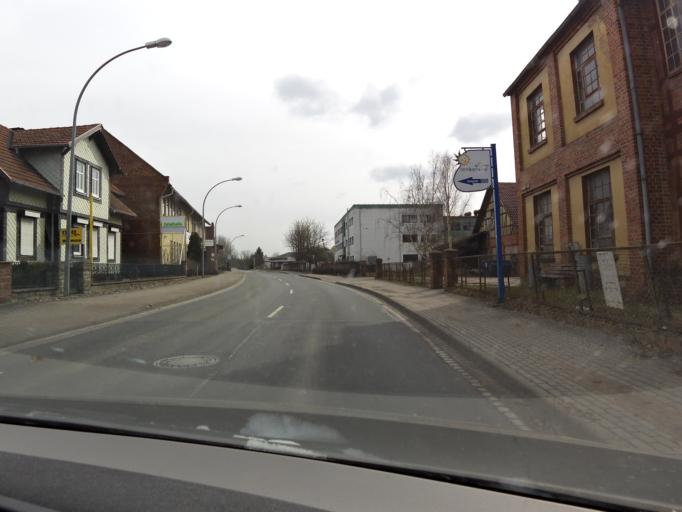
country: DE
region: Thuringia
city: Barchfeld
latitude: 50.7954
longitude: 10.3008
